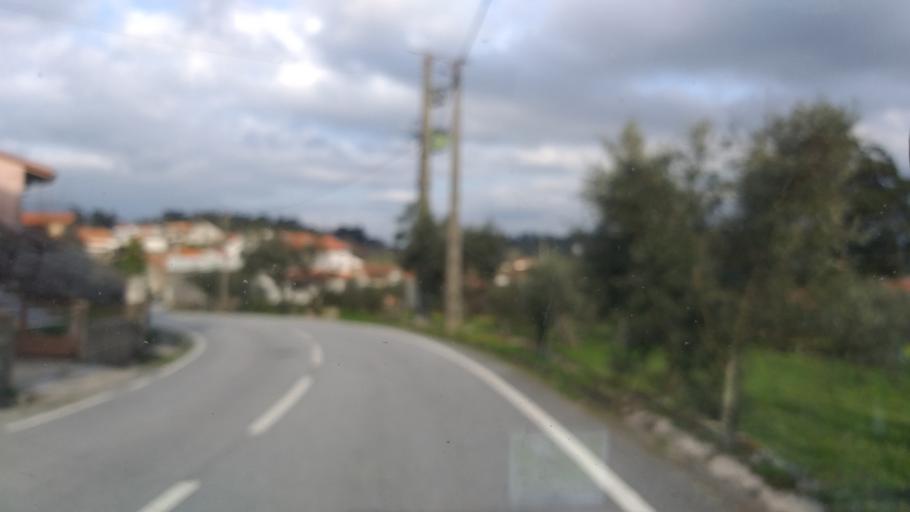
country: PT
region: Guarda
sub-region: Manteigas
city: Manteigas
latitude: 40.5127
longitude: -7.6084
